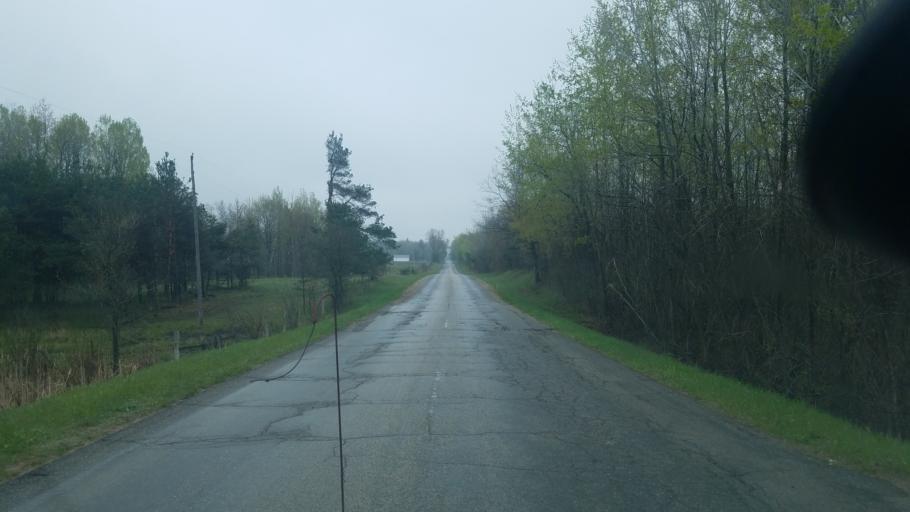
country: US
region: Michigan
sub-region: Mecosta County
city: Canadian Lakes
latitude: 43.5762
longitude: -85.3936
